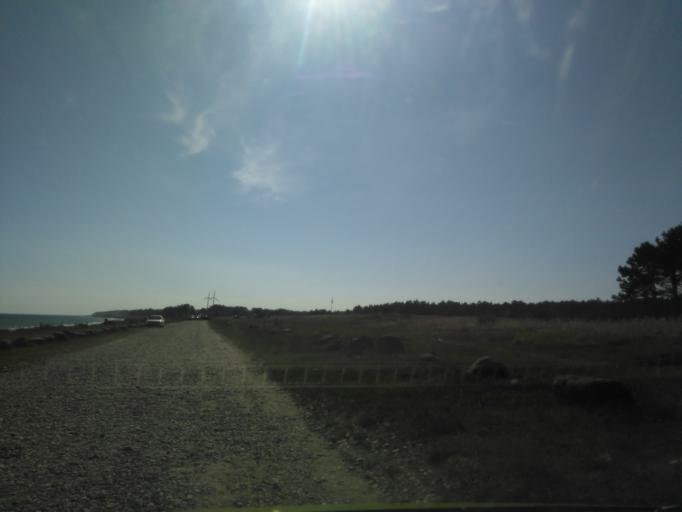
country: DK
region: Central Jutland
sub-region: Syddjurs Kommune
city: Ebeltoft
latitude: 56.2045
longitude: 10.7335
